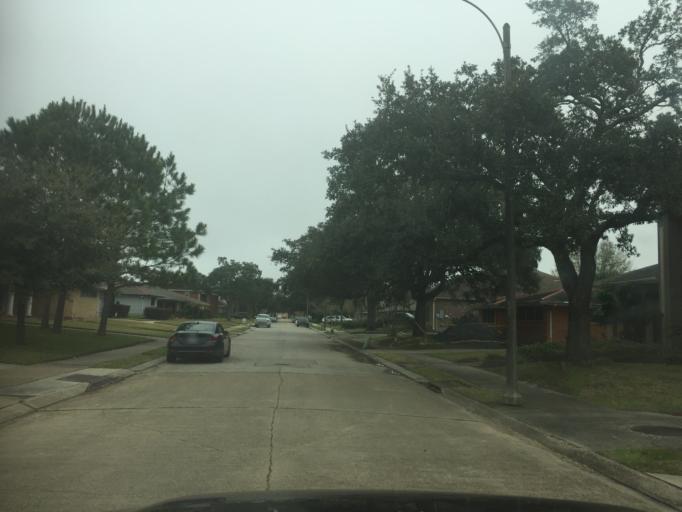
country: US
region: Louisiana
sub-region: Jefferson Parish
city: Metairie
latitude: 30.0201
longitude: -90.1030
